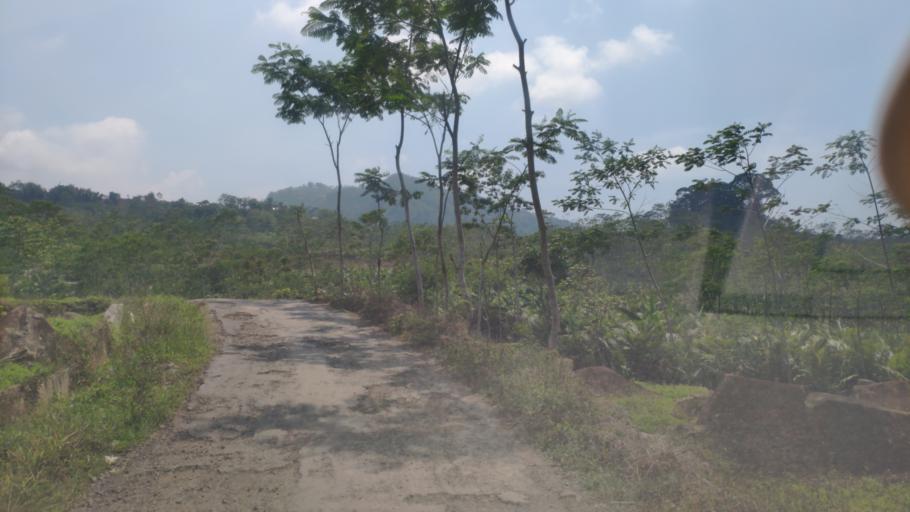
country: ID
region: Central Java
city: Wonosobo
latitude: -7.2910
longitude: 109.6933
